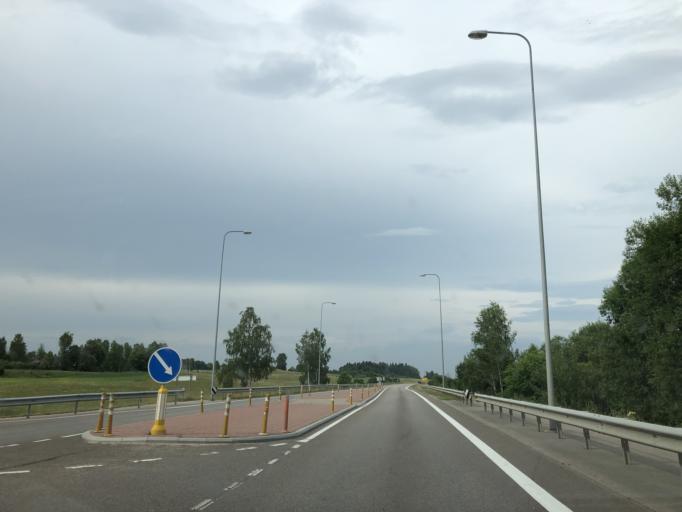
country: LT
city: Moletai
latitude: 55.1322
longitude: 25.3938
